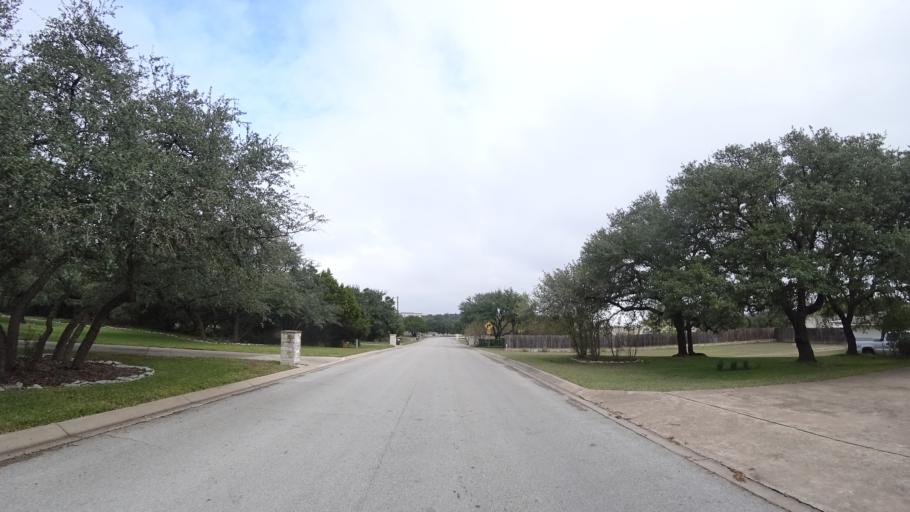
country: US
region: Texas
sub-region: Travis County
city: Shady Hollow
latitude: 30.2201
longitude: -97.8952
